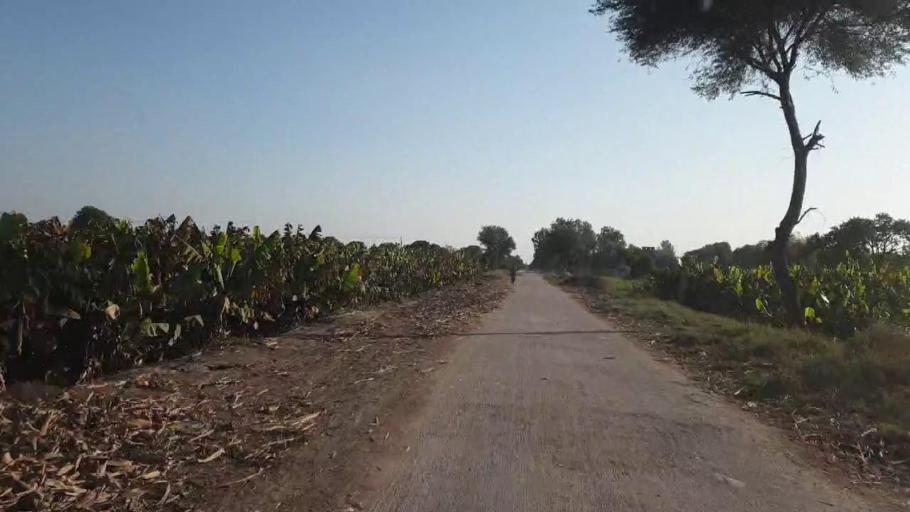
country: PK
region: Sindh
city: Tando Allahyar
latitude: 25.3695
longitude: 68.6825
